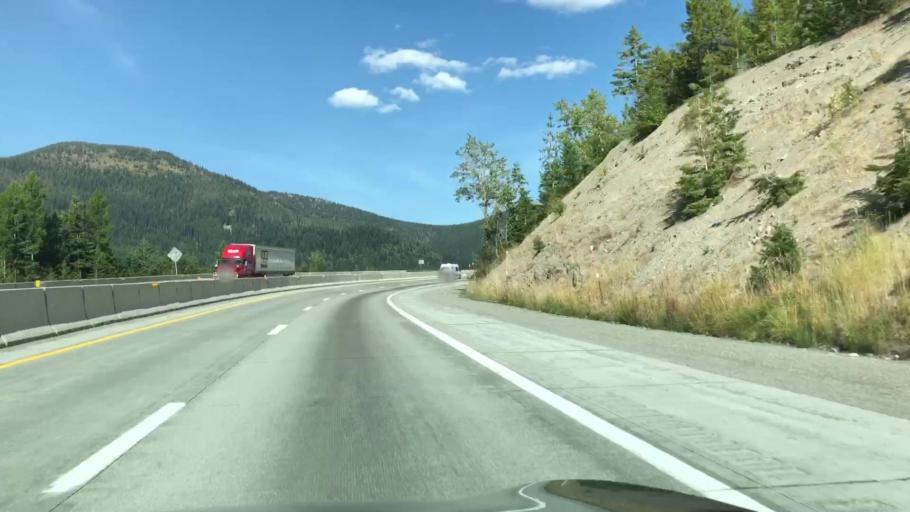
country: US
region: Idaho
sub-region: Shoshone County
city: Wallace
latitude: 47.4618
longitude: -115.7110
